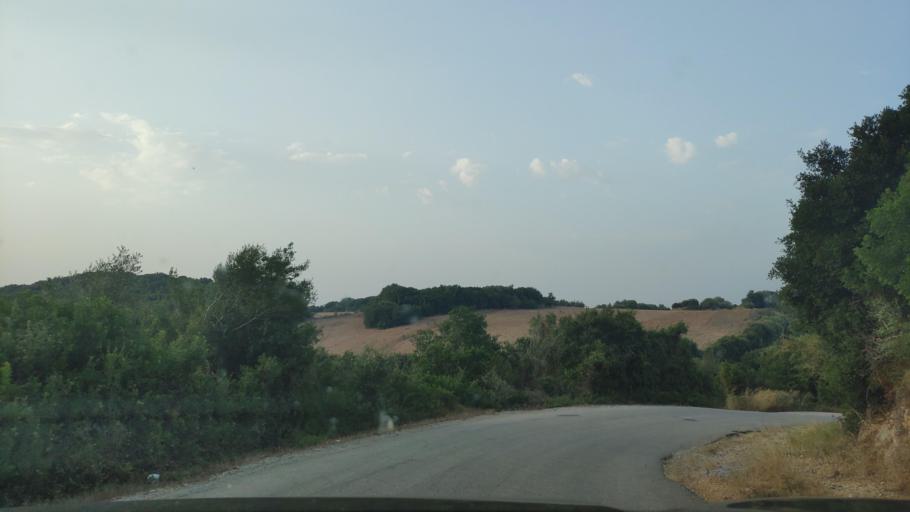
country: GR
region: West Greece
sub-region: Nomos Aitolias kai Akarnanias
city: Monastirakion
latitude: 38.9220
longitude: 20.9803
